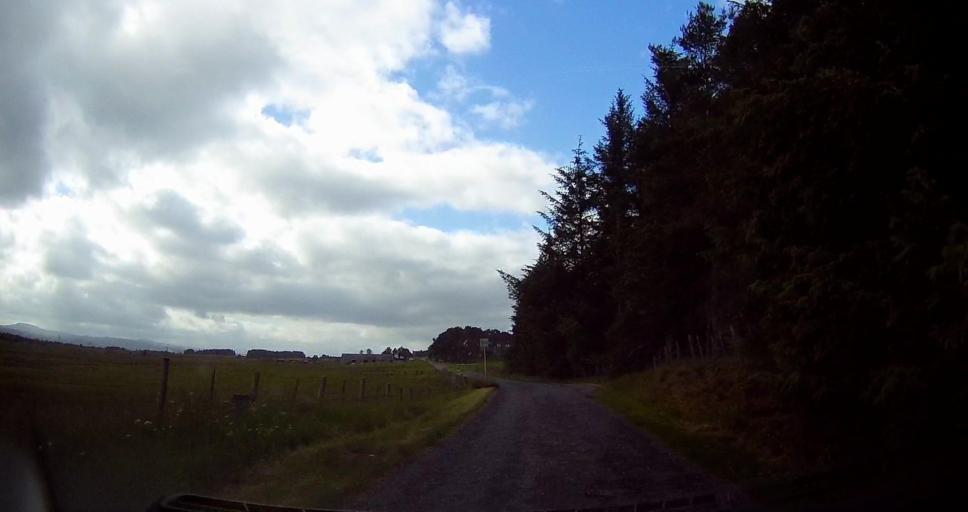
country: GB
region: Scotland
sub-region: Highland
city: Alness
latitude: 58.0689
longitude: -4.4279
